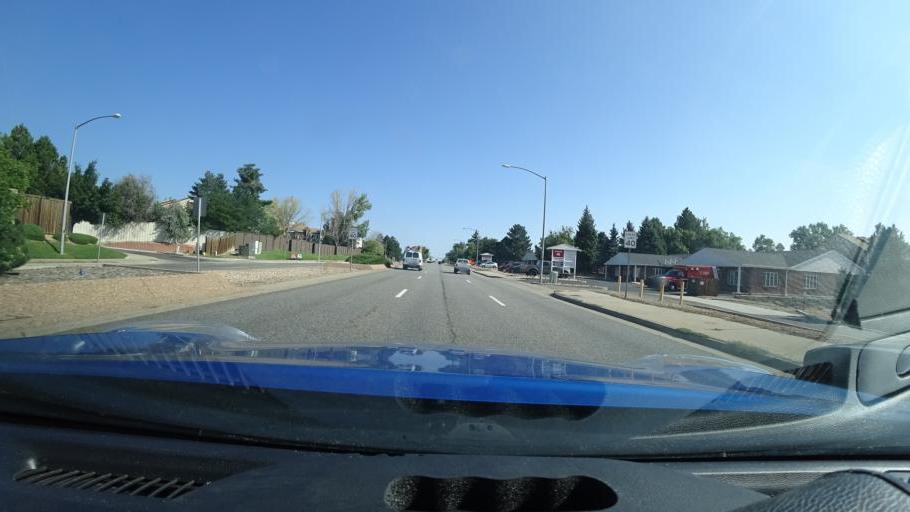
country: US
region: Colorado
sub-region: Adams County
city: Aurora
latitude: 39.6921
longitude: -104.8098
